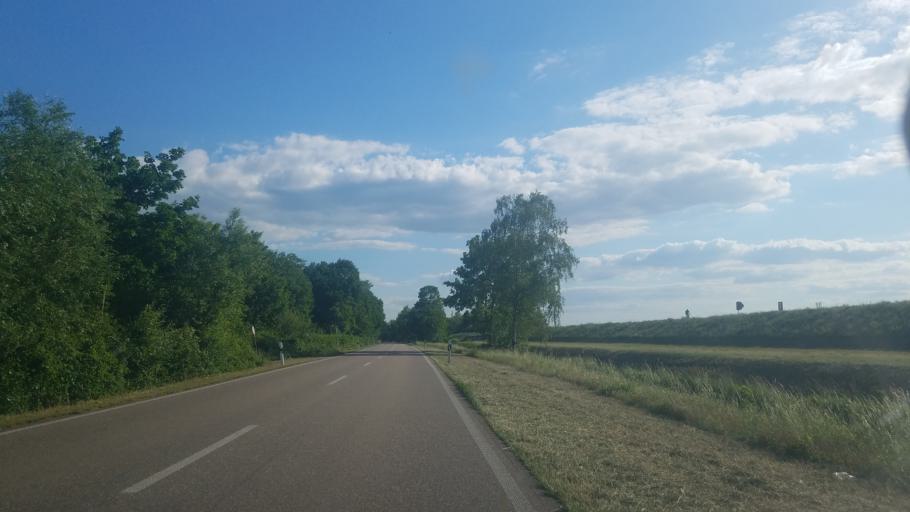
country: FR
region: Alsace
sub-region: Departement du Bas-Rhin
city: La Wantzenau
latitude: 48.6148
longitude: 7.8295
